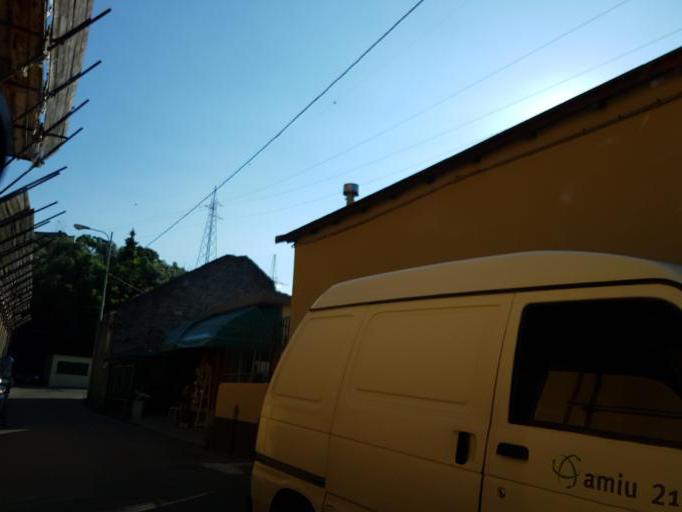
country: IT
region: Liguria
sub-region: Provincia di Genova
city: San Teodoro
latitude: 44.4275
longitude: 8.8679
